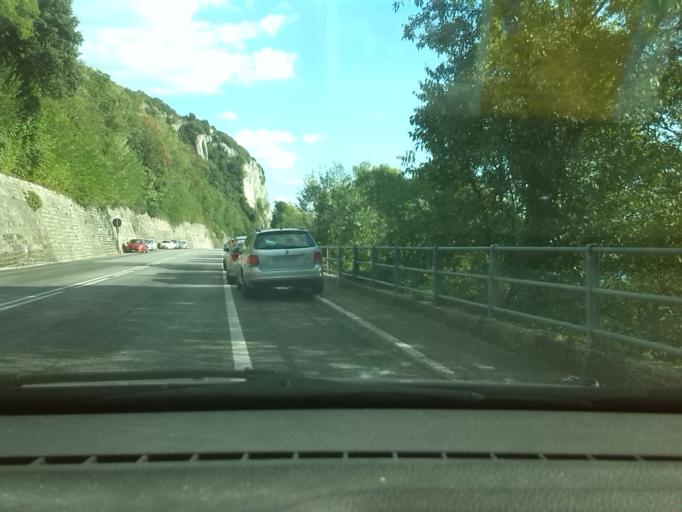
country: IT
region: Friuli Venezia Giulia
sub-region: Provincia di Trieste
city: Aurisina Cave
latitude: 45.7497
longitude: 13.6588
